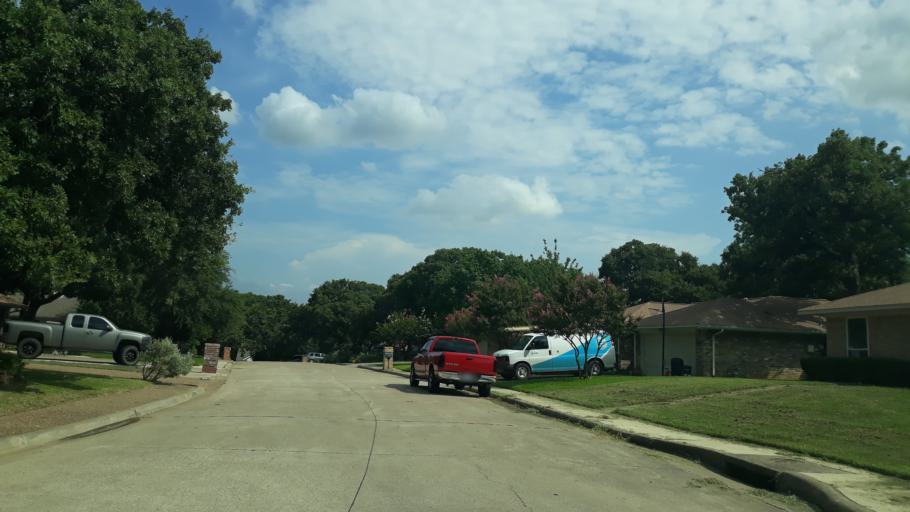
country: US
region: Texas
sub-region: Dallas County
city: Irving
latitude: 32.8132
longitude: -96.9983
